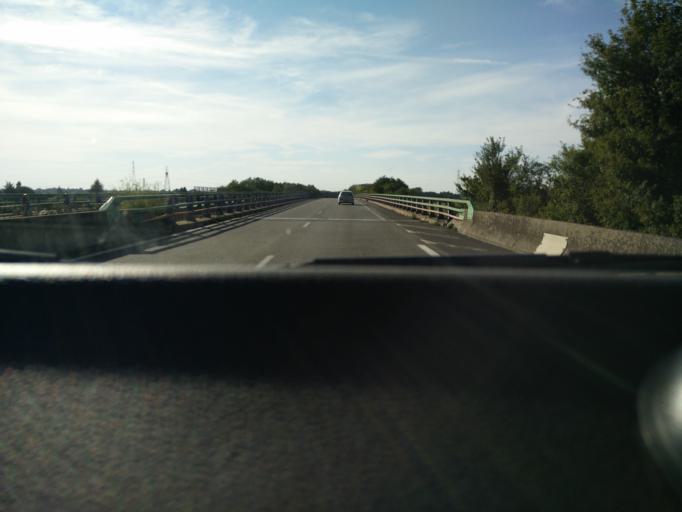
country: FR
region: Nord-Pas-de-Calais
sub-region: Departement du Nord
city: Escaudain
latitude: 50.3280
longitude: 3.3354
